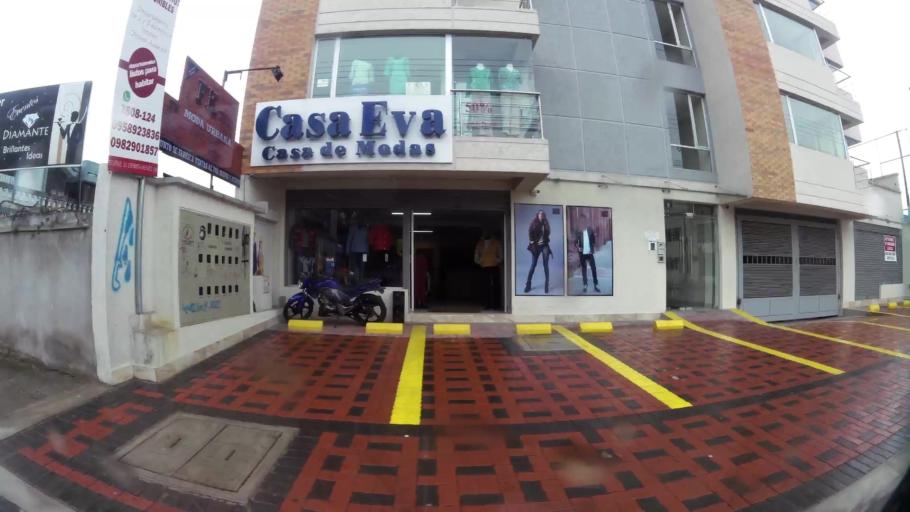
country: EC
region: Pichincha
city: Sangolqui
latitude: -0.3056
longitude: -78.4505
